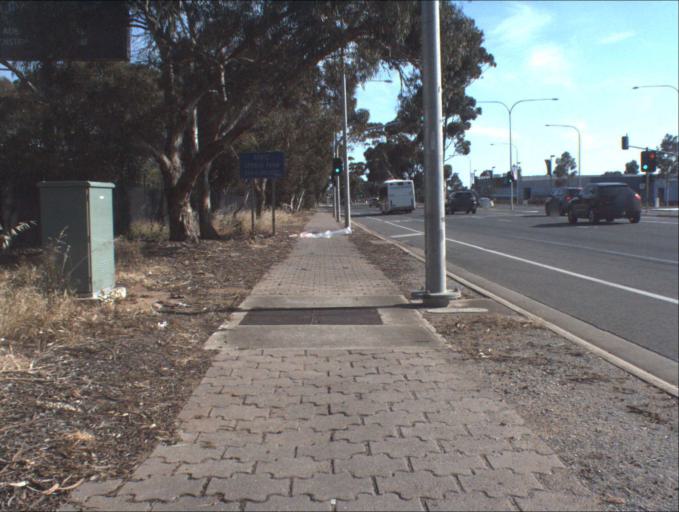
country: AU
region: South Australia
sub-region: Port Adelaide Enfield
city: Enfield
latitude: -34.8372
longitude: 138.6084
